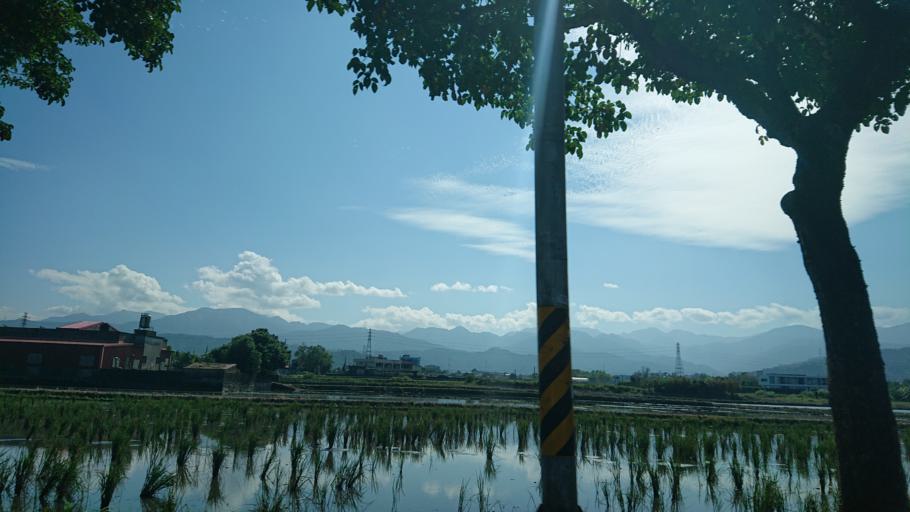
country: TW
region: Taiwan
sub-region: Yilan
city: Yilan
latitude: 24.6699
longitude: 121.7217
